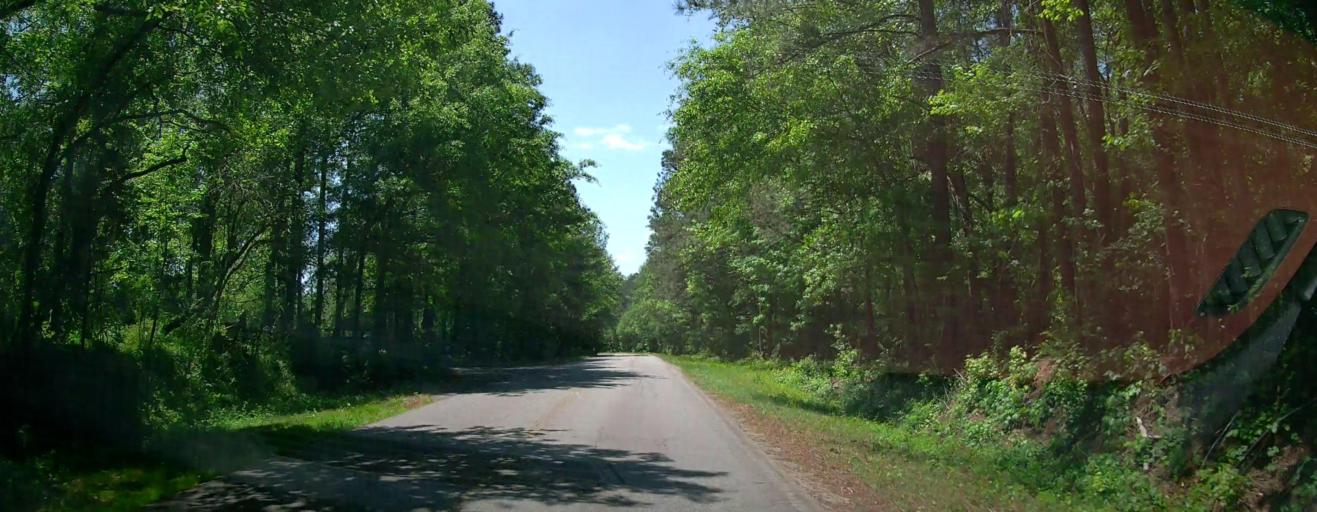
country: US
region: Georgia
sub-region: Jasper County
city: Monticello
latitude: 33.2848
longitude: -83.6952
